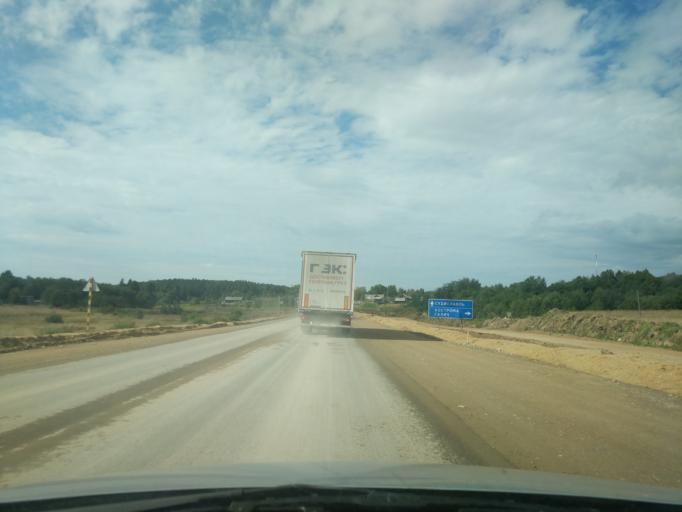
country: RU
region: Kostroma
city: Sudislavl'
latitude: 57.8749
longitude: 41.7344
